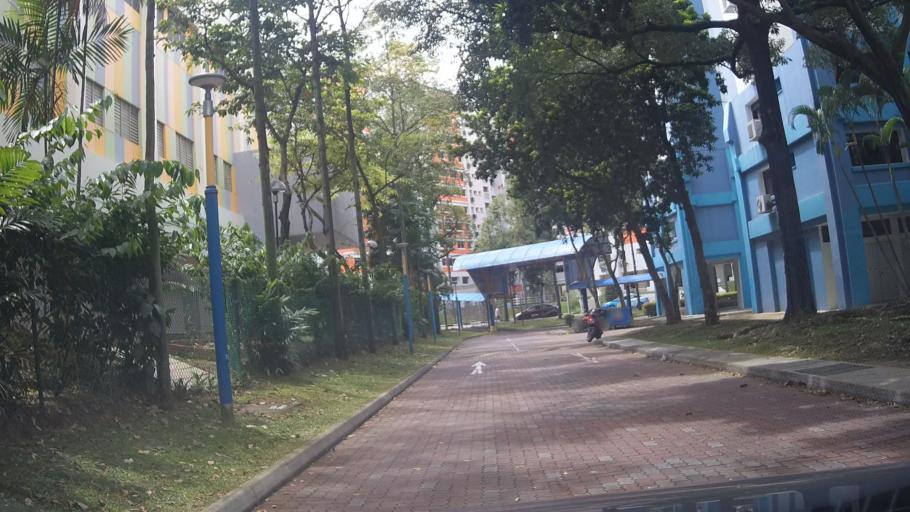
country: MY
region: Johor
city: Johor Bahru
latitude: 1.4443
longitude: 103.7947
